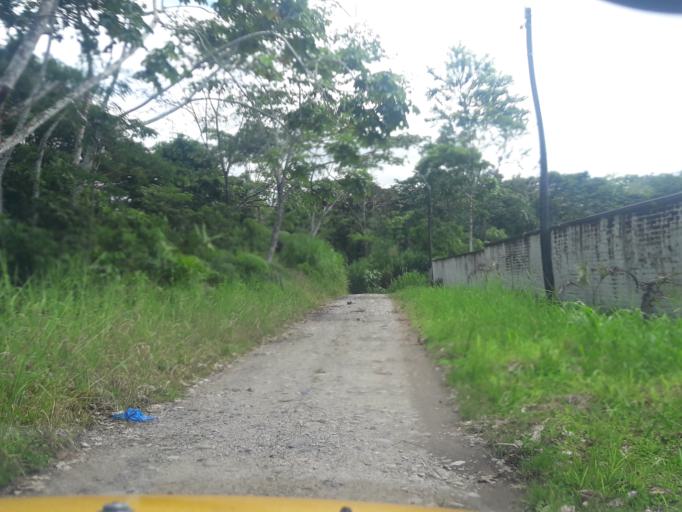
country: EC
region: Napo
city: Tena
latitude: -1.0067
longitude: -77.8224
